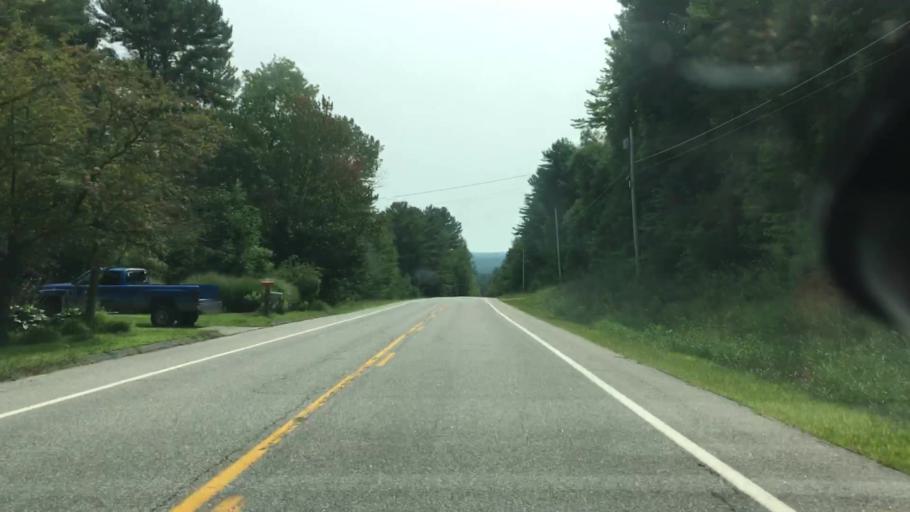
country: US
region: Maine
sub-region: Kennebec County
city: Wayne
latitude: 44.3754
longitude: -70.0976
